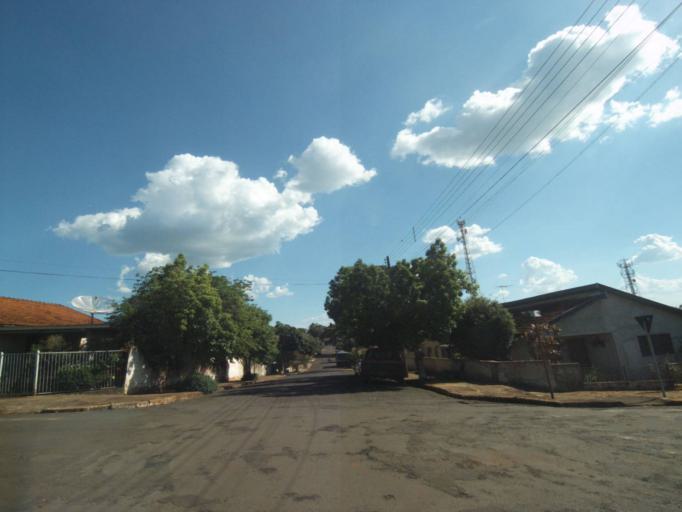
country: BR
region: Parana
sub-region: Sertanopolis
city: Sertanopolis
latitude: -23.0391
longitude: -50.8158
